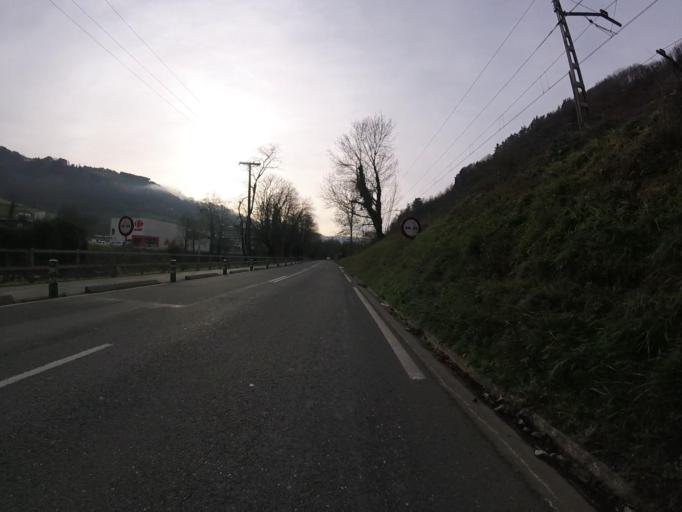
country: ES
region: Basque Country
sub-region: Provincia de Guipuzcoa
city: Tolosa
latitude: 43.1479
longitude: -2.0724
